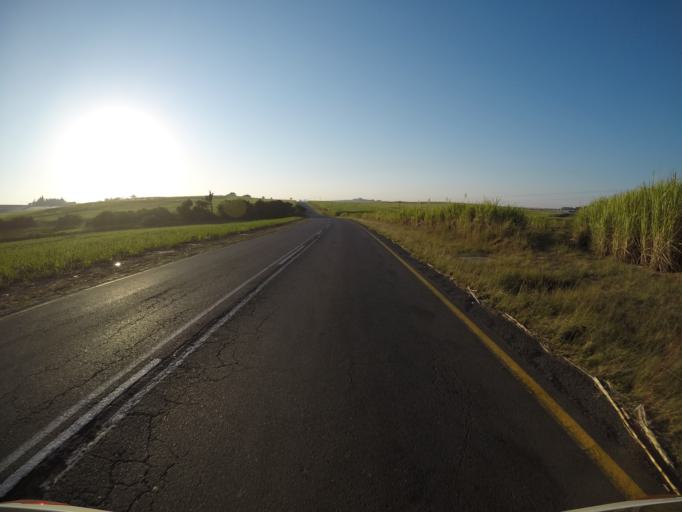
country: ZA
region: KwaZulu-Natal
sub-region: uThungulu District Municipality
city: eSikhawini
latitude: -28.9494
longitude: 31.7031
